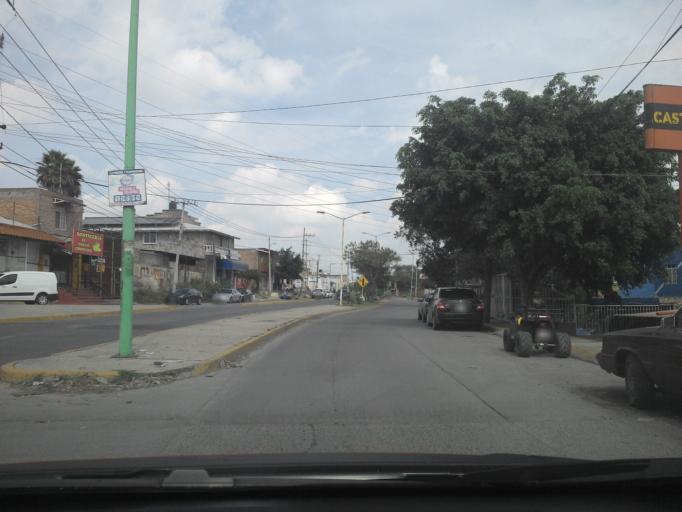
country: MX
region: Jalisco
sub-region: Tlajomulco de Zuniga
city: Altus Bosques
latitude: 20.5889
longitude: -103.3509
